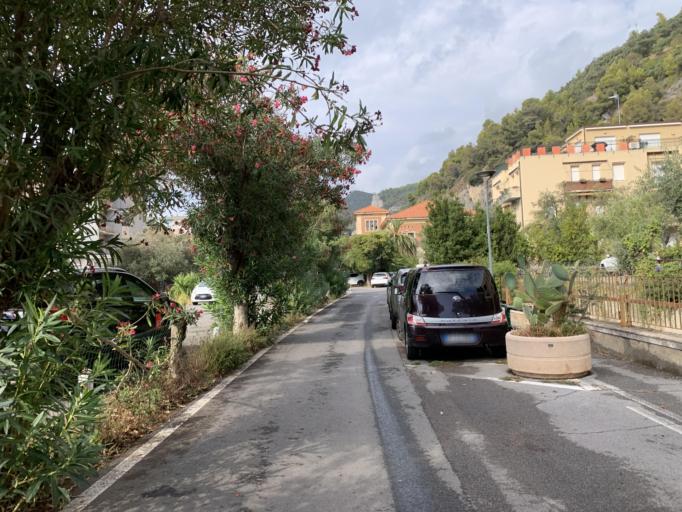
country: IT
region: Liguria
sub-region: Provincia di Savona
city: Noli
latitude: 44.1824
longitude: 8.3992
